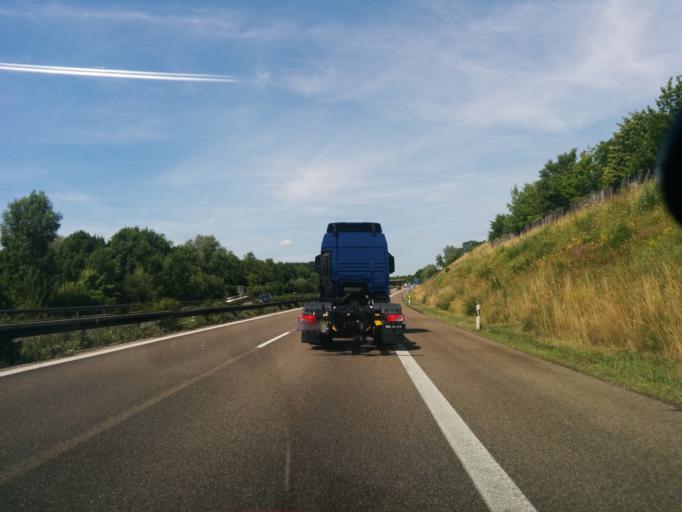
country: DE
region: Bavaria
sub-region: Upper Bavaria
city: Eching
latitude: 48.0757
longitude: 11.1062
